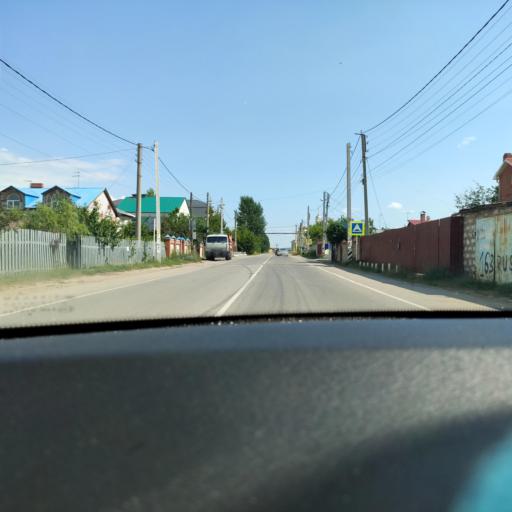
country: RU
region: Samara
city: Volzhskiy
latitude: 53.4506
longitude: 50.1744
